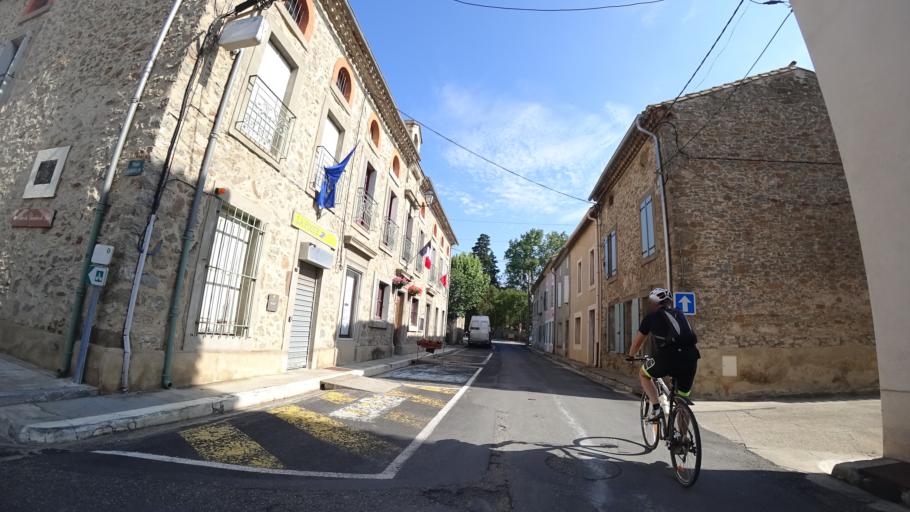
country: FR
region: Languedoc-Roussillon
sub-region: Departement de l'Herault
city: Olonzac
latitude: 43.2674
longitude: 2.7209
